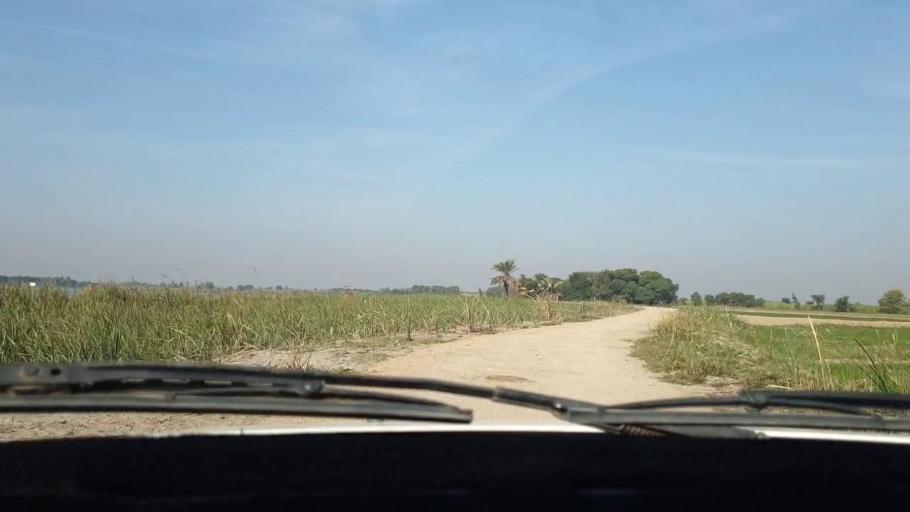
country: PK
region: Sindh
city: Tando Muhammad Khan
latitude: 24.9998
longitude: 68.4617
